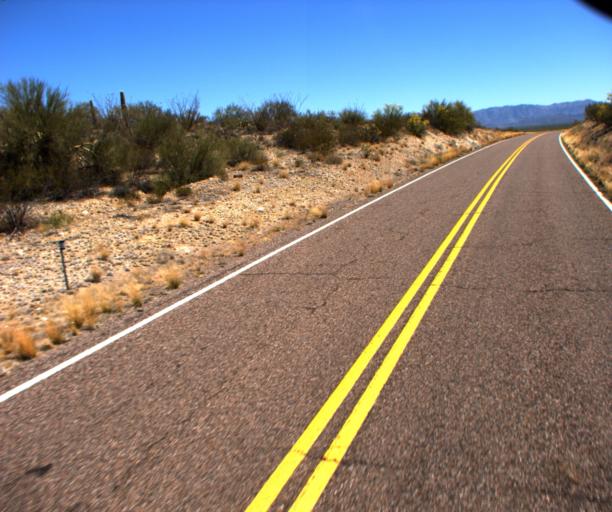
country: US
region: Arizona
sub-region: Yavapai County
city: Congress
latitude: 34.1069
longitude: -112.9913
